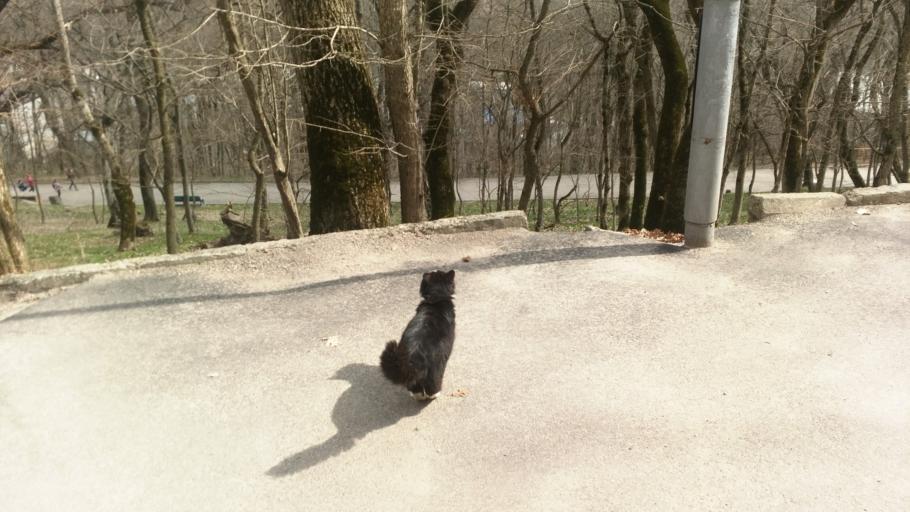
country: RU
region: Stavropol'skiy
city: Zheleznovodsk
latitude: 44.1355
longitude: 43.0365
